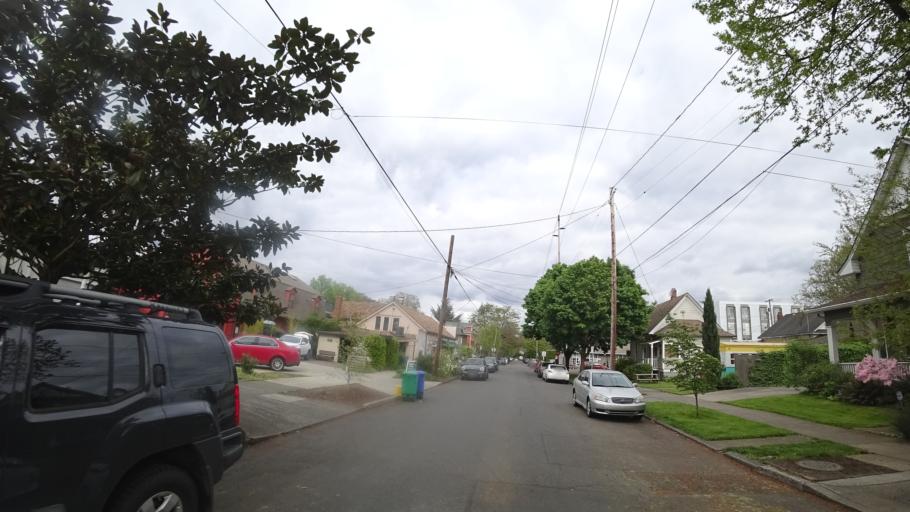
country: US
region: Oregon
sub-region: Clackamas County
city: Milwaukie
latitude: 45.4657
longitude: -122.6539
